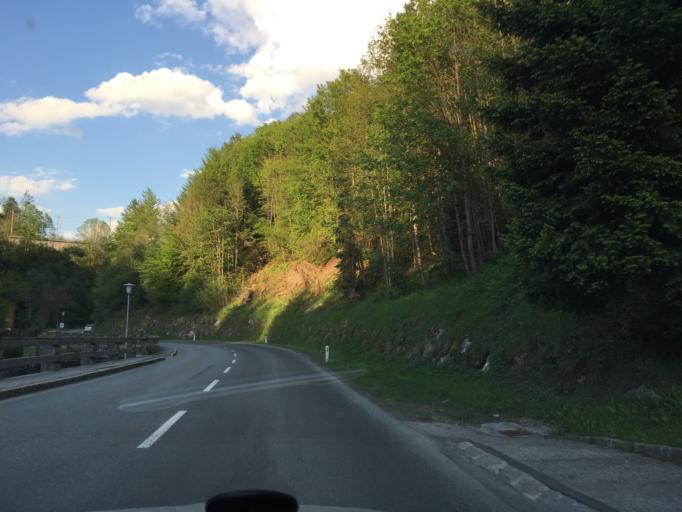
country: AT
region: Tyrol
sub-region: Politischer Bezirk Kitzbuhel
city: Fieberbrunn
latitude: 47.4880
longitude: 12.5325
